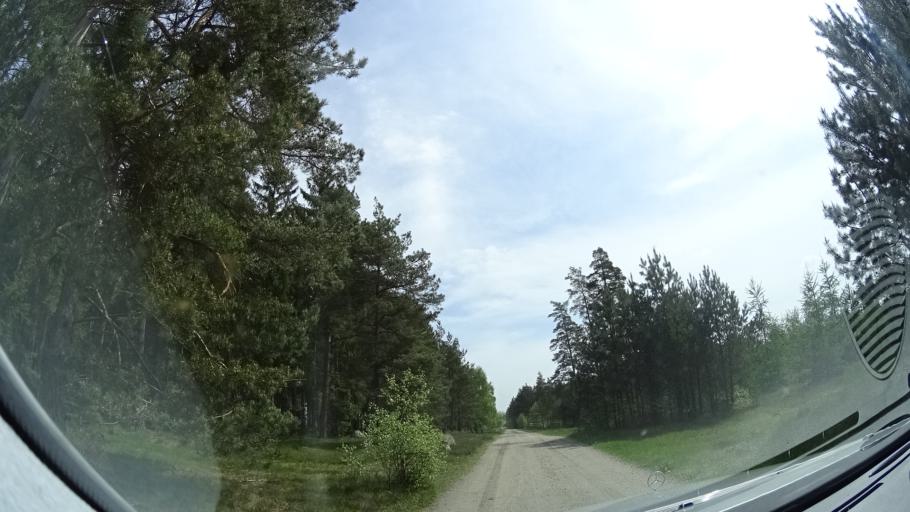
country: SE
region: Skane
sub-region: Sjobo Kommun
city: Sjoebo
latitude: 55.6680
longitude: 13.6475
